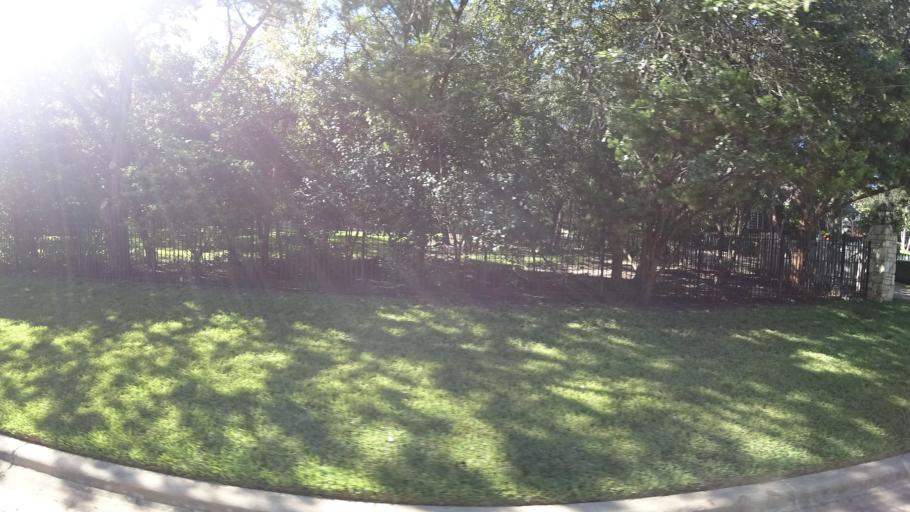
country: US
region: Texas
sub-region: Travis County
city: West Lake Hills
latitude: 30.3343
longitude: -97.7875
